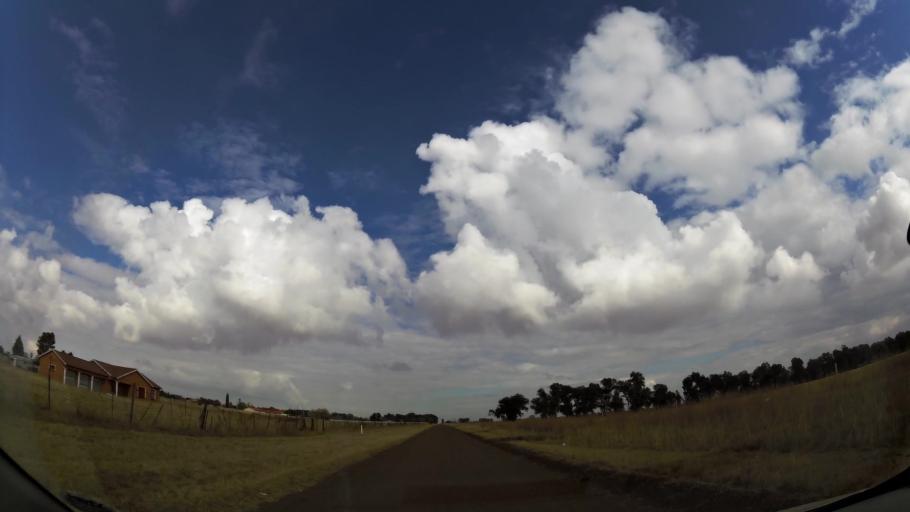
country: ZA
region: Gauteng
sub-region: Sedibeng District Municipality
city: Meyerton
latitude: -26.5973
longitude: 28.0880
